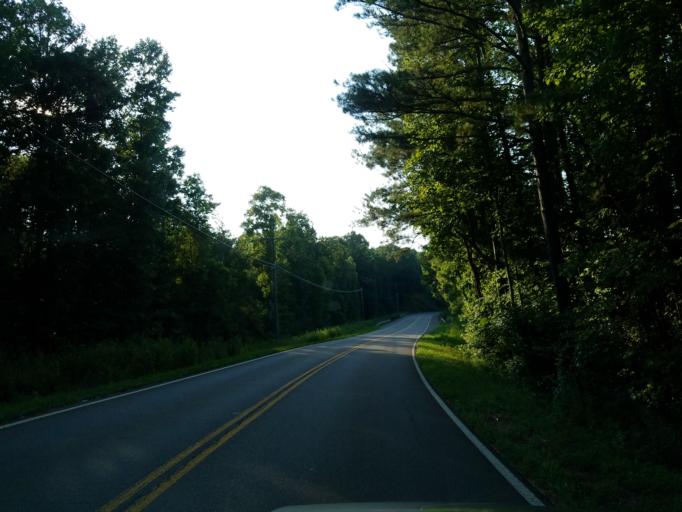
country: US
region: Georgia
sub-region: Pickens County
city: Jasper
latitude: 34.5410
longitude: -84.5403
